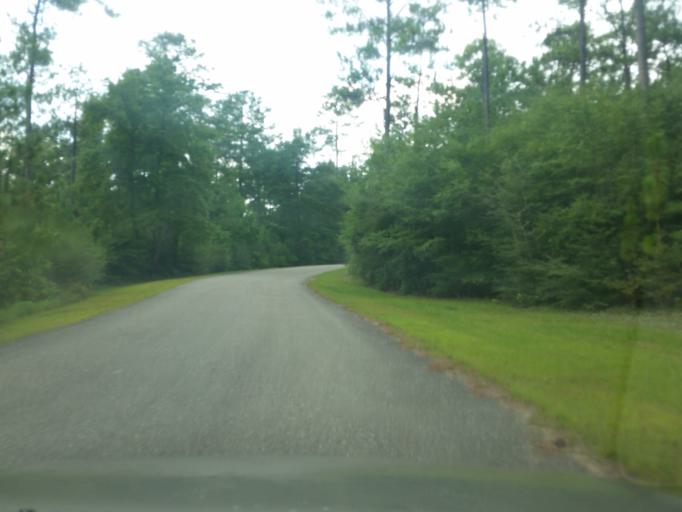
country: US
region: Alabama
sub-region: Baldwin County
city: Spanish Fort
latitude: 30.7372
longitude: -87.9063
